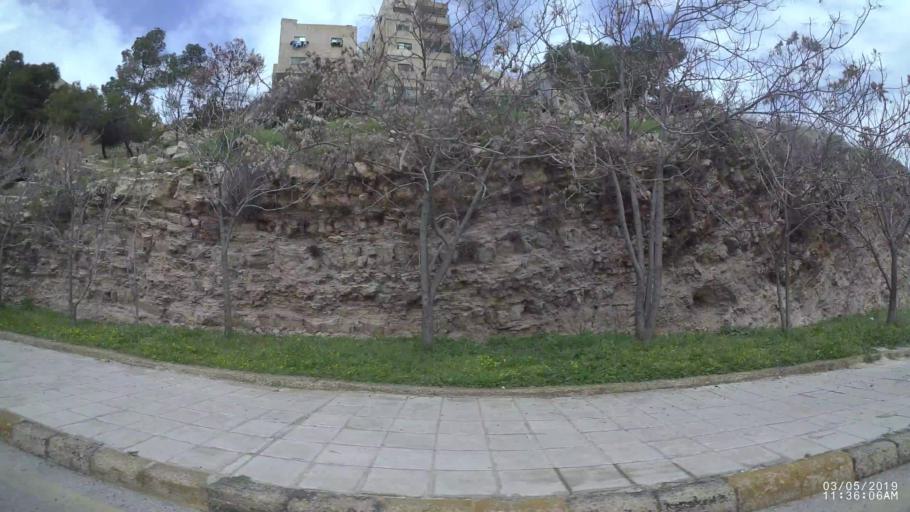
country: JO
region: Amman
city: Amman
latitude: 31.9597
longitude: 35.9549
